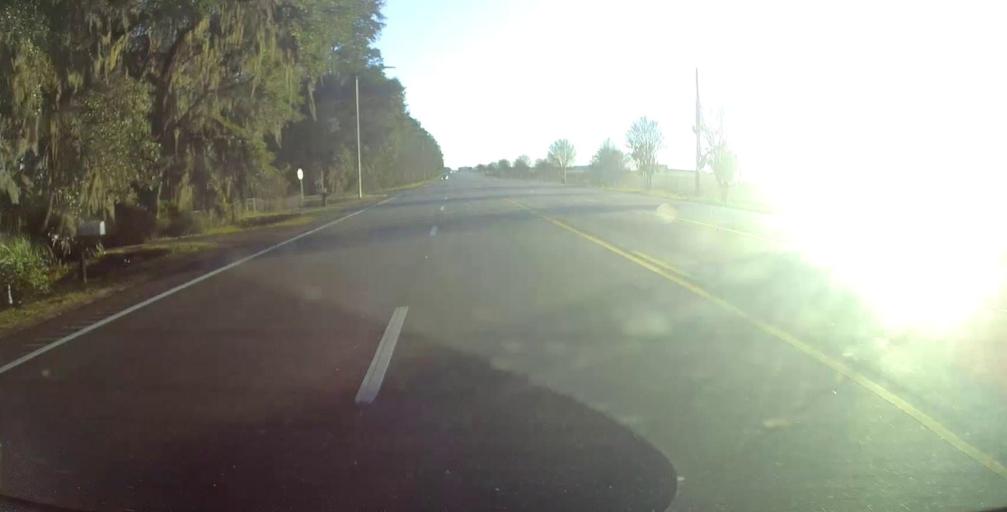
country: US
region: Georgia
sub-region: Dougherty County
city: Albany
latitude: 31.5407
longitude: -84.1807
